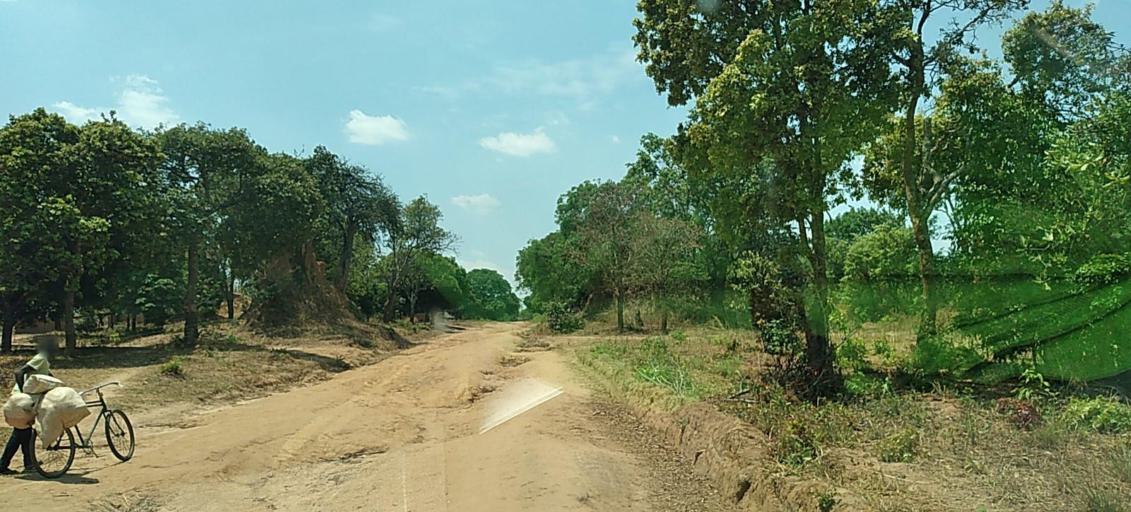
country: CD
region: Katanga
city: Kolwezi
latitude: -11.3223
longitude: 25.2293
